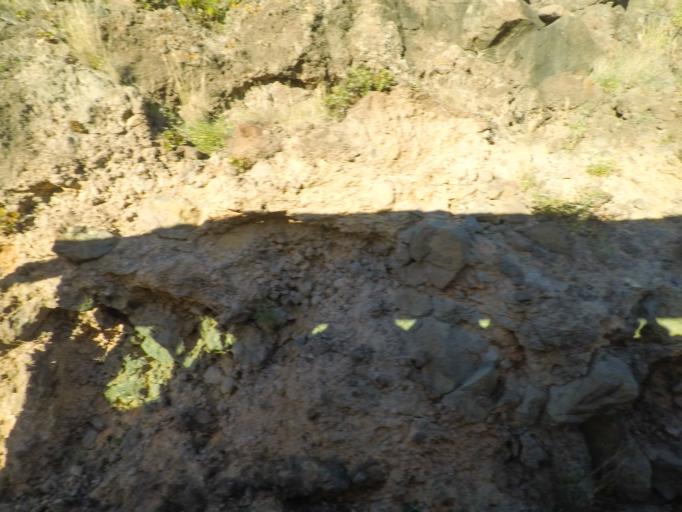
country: ES
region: Canary Islands
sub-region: Provincia de Santa Cruz de Tenerife
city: San Sebastian de la Gomera
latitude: 28.0944
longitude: -17.1541
